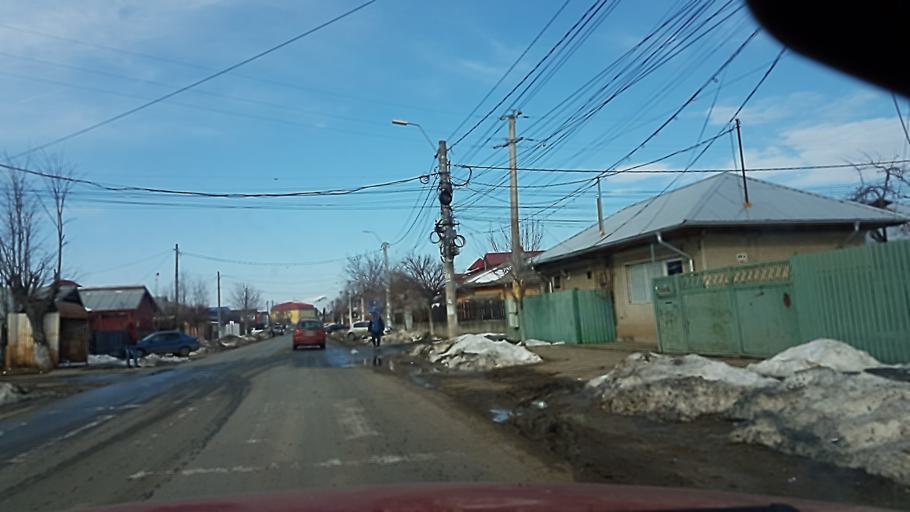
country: RO
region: Ilfov
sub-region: Comuna Tunari
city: Tunari
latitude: 44.5449
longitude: 26.1421
